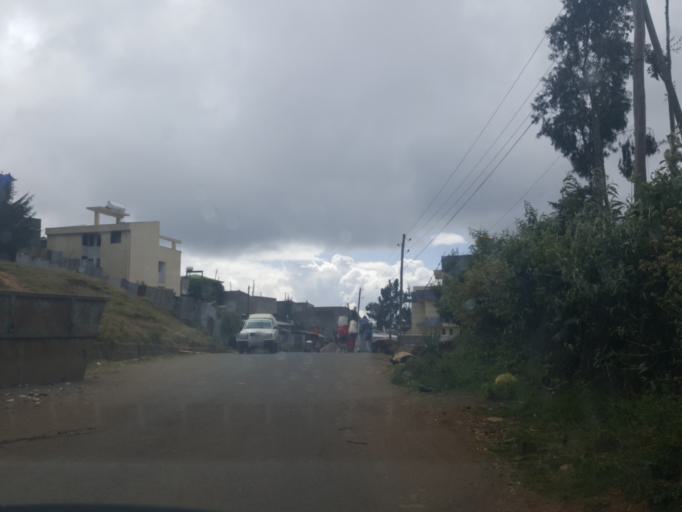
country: ET
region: Adis Abeba
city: Addis Ababa
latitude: 9.0692
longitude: 38.7395
